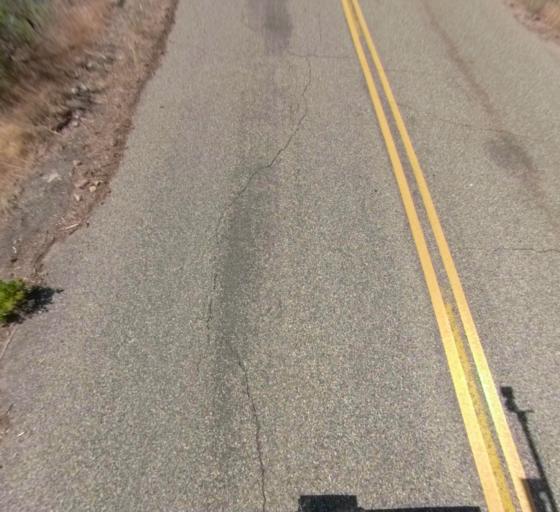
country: US
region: California
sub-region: Fresno County
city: Auberry
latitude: 37.3105
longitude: -119.3483
